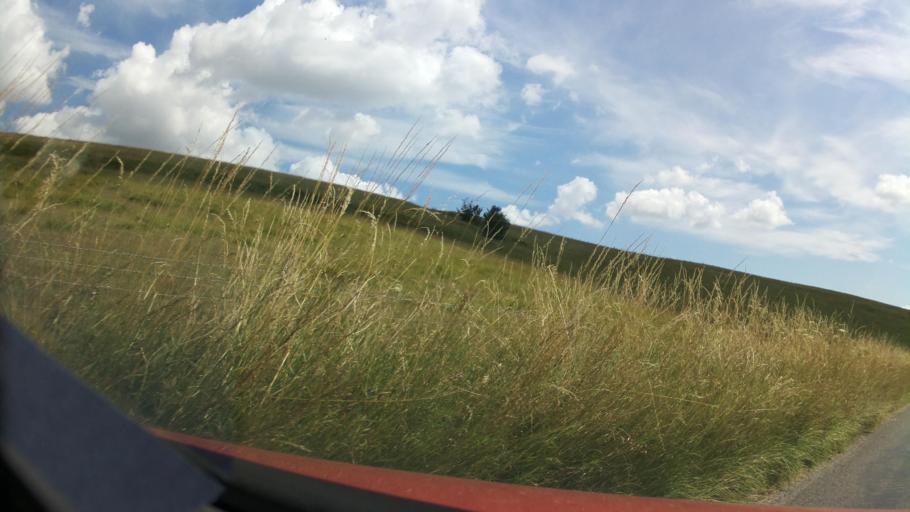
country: GB
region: England
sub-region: Wiltshire
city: Aldbourne
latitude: 51.5330
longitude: -1.5877
